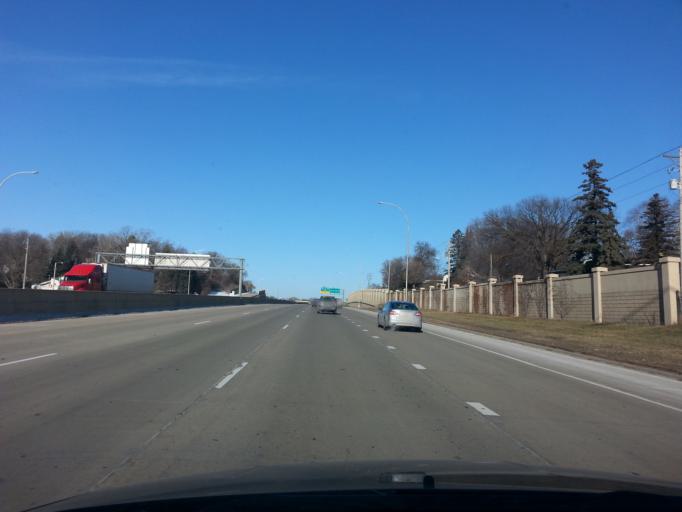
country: US
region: Minnesota
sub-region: Olmsted County
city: Rochester
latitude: 44.0122
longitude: -92.4842
